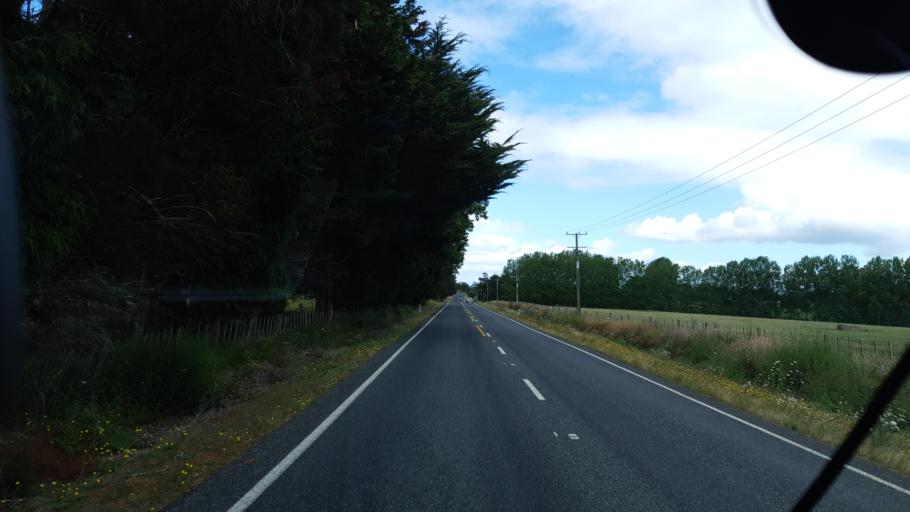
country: NZ
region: Northland
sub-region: Far North District
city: Waimate North
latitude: -35.3204
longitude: 173.7866
